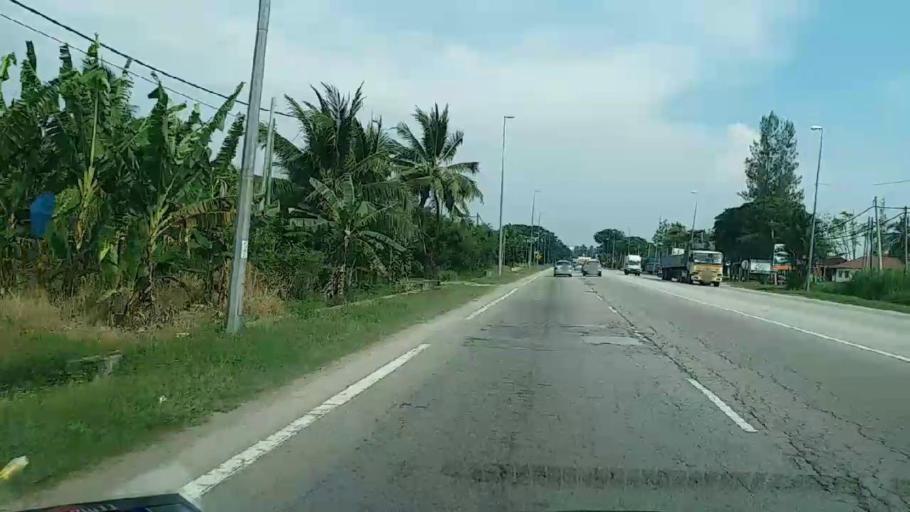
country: MY
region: Selangor
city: Kuala Selangor
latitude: 3.3598
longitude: 101.2496
